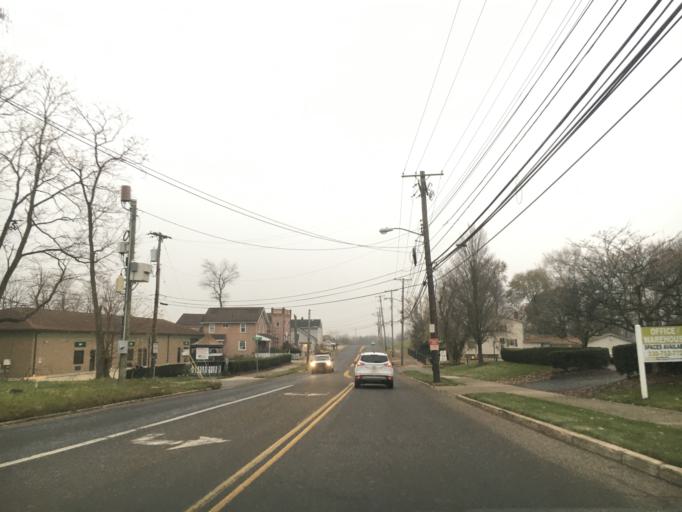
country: US
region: Ohio
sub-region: Summit County
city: Akron
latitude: 41.0945
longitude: -81.4880
